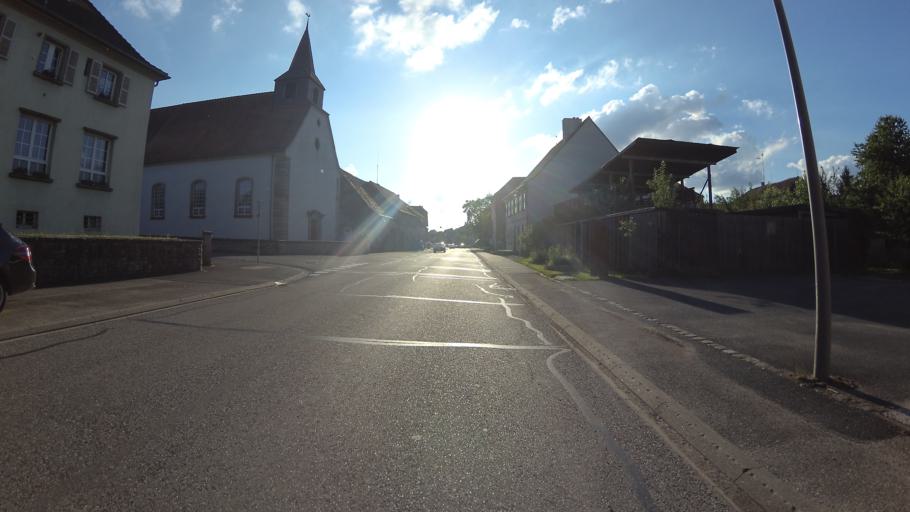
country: FR
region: Alsace
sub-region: Departement du Bas-Rhin
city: Diemeringen
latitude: 48.9521
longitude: 7.1778
